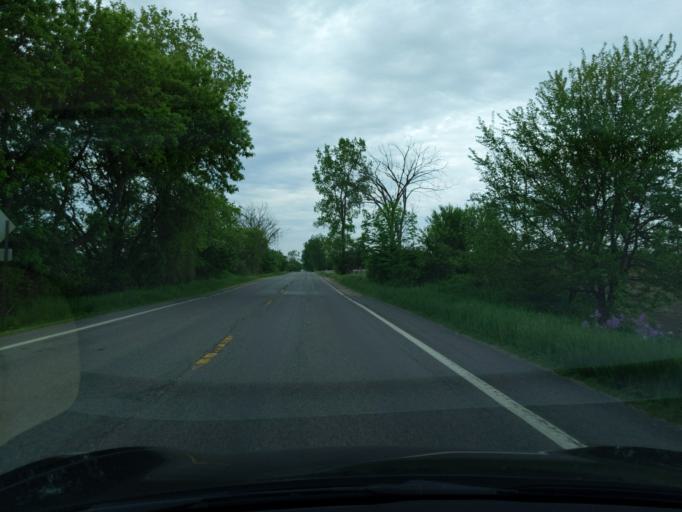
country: US
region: Michigan
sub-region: Ingham County
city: Mason
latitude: 42.6022
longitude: -84.3578
